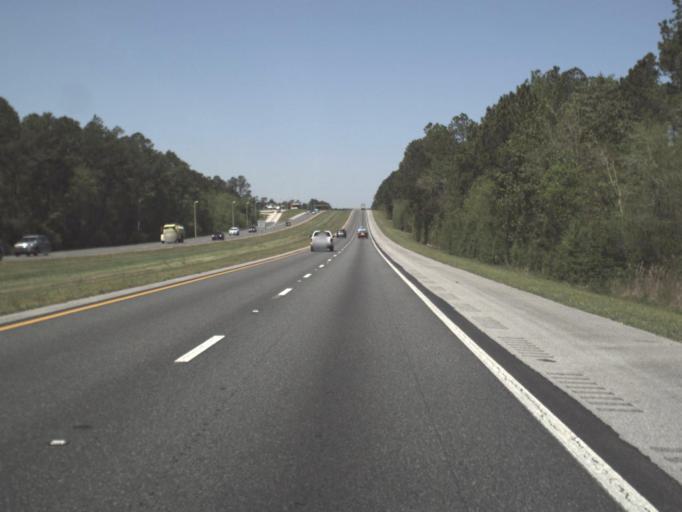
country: US
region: Florida
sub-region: Escambia County
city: Cantonment
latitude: 30.5668
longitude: -87.3896
